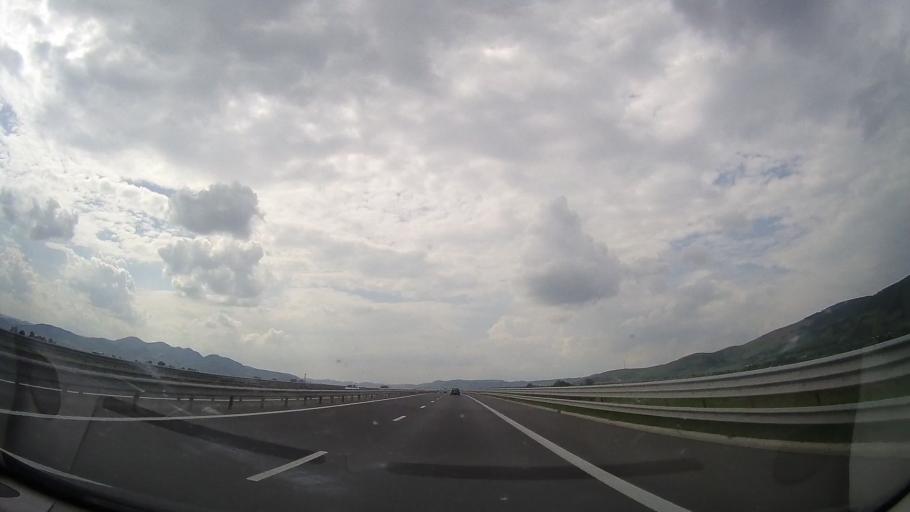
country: RO
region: Hunedoara
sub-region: Oras Simeria
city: Simeria
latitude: 45.8826
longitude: 22.9901
